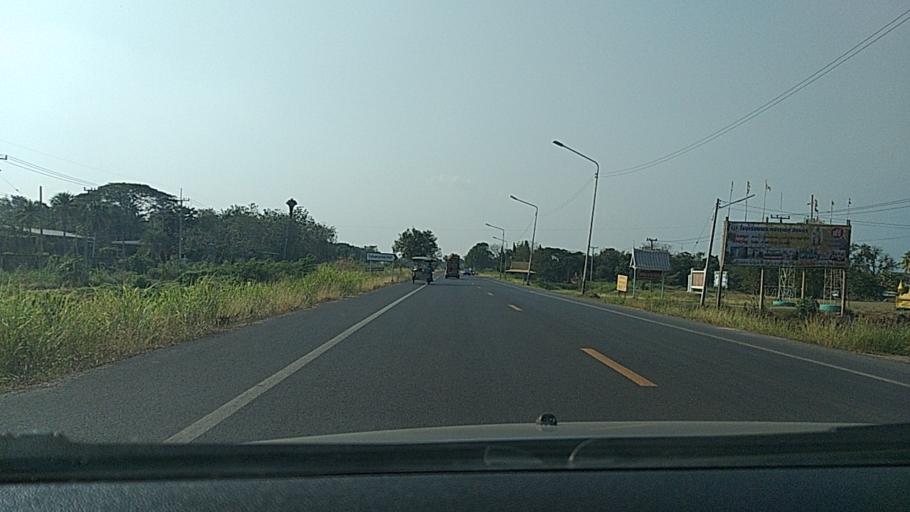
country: TH
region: Sing Buri
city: Phrom Buri
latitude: 14.7984
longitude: 100.4408
